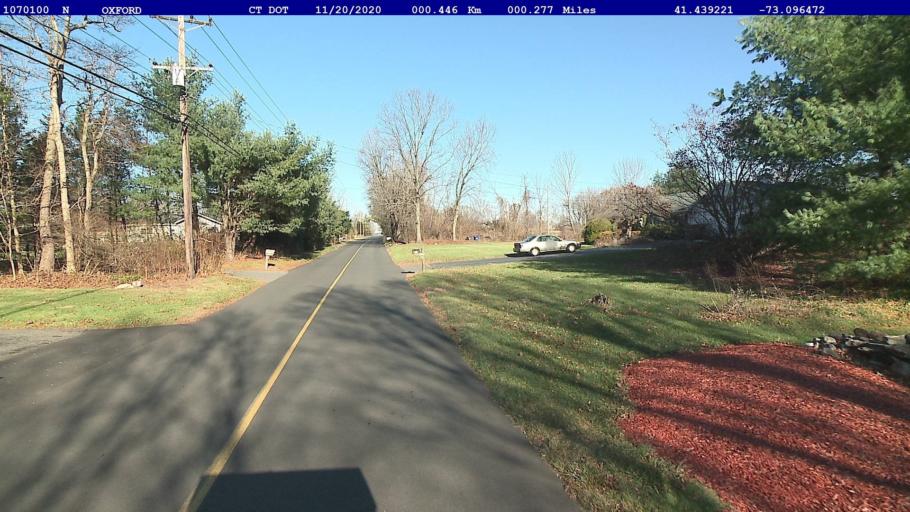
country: US
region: Connecticut
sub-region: New Haven County
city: Oxford
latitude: 41.4392
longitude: -73.0965
